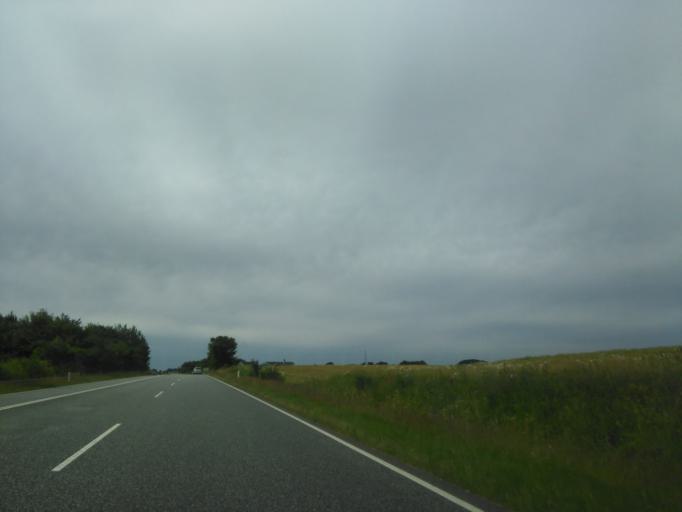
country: DK
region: Central Jutland
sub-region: Arhus Kommune
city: Solbjerg
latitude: 56.0325
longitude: 10.0668
